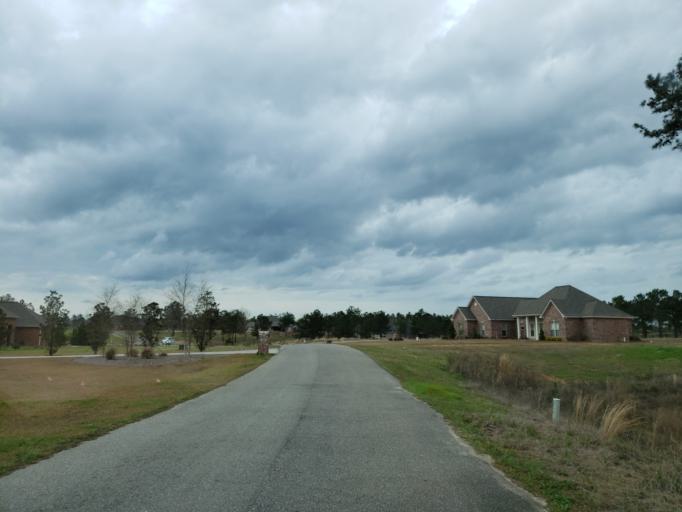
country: US
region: Mississippi
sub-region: Jones County
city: Ellisville
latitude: 31.5548
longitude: -89.2556
